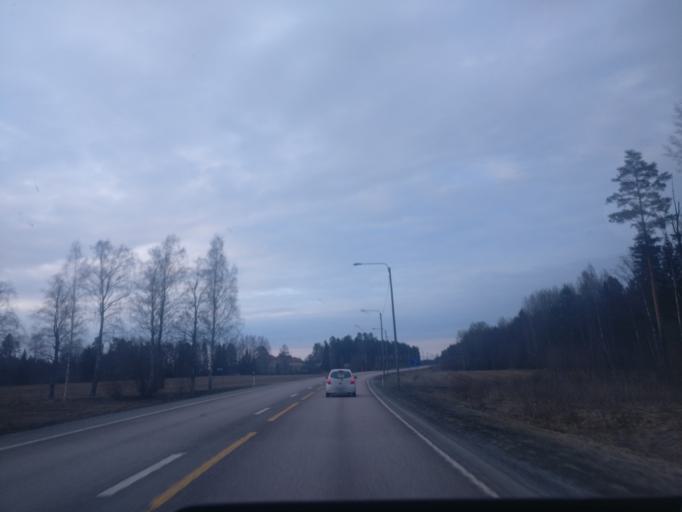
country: FI
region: Paijanne Tavastia
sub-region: Lahti
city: Hartola
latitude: 61.5006
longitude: 25.9804
